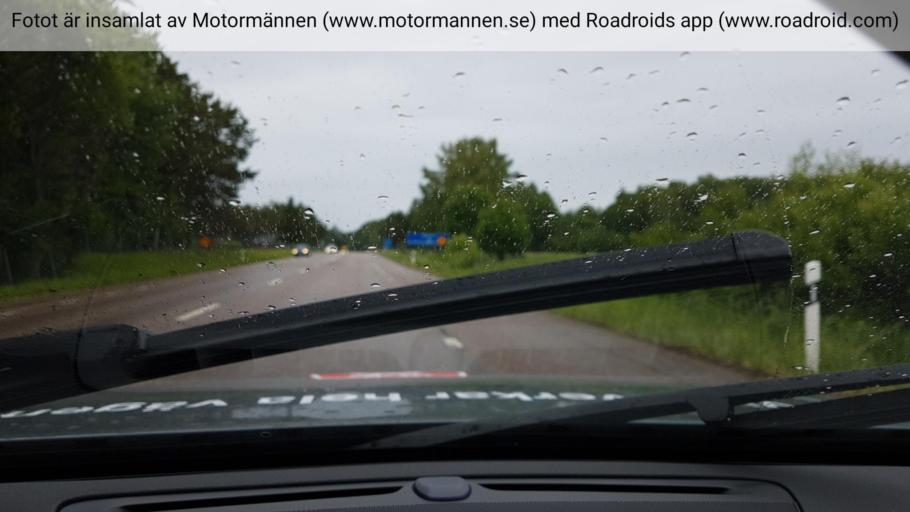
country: SE
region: Uppsala
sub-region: Alvkarleby Kommun
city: AElvkarleby
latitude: 60.5817
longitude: 17.4655
